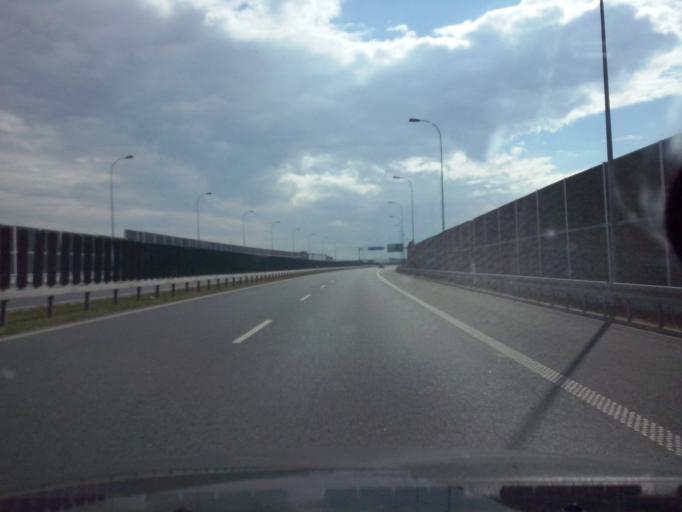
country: PL
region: Lesser Poland Voivodeship
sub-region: Powiat tarnowski
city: Wierzchoslawice
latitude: 50.0183
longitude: 20.8718
